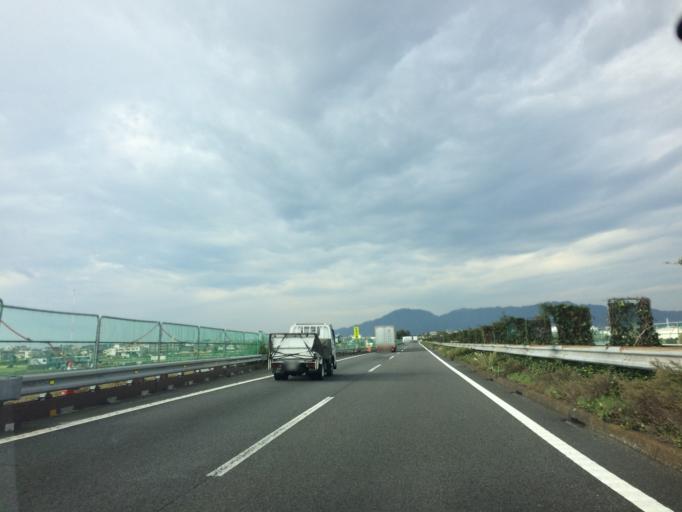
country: JP
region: Shizuoka
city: Shizuoka-shi
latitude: 34.9626
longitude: 138.4237
